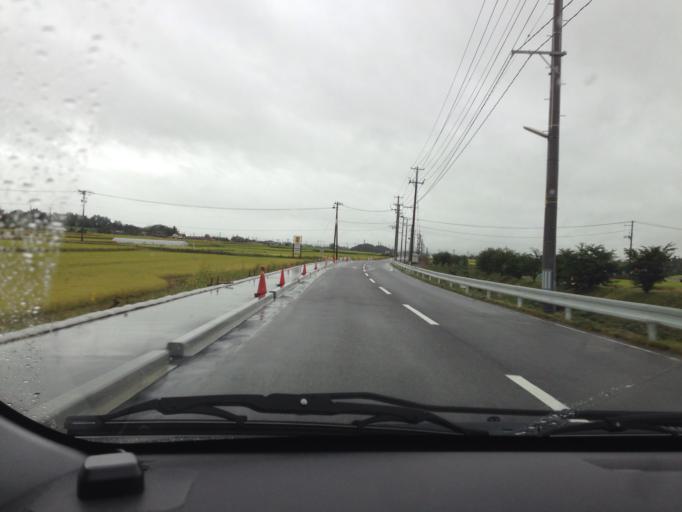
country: JP
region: Fukushima
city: Koriyama
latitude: 37.4548
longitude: 140.3036
